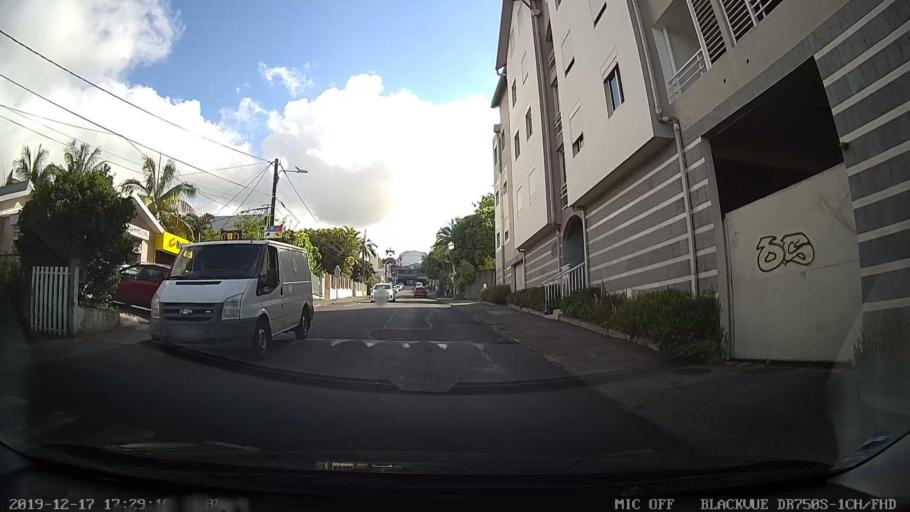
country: RE
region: Reunion
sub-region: Reunion
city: Le Tampon
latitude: -21.2798
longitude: 55.5139
